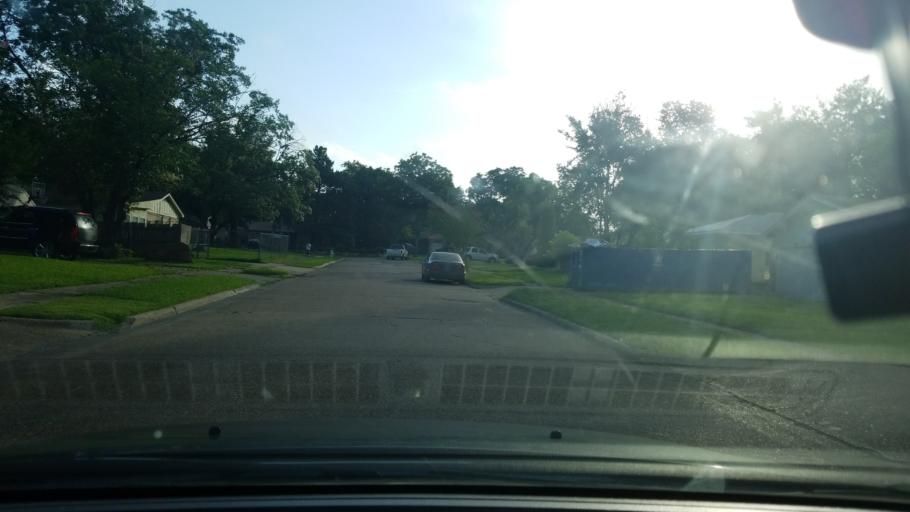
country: US
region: Texas
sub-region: Dallas County
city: Mesquite
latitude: 32.8282
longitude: -96.6478
